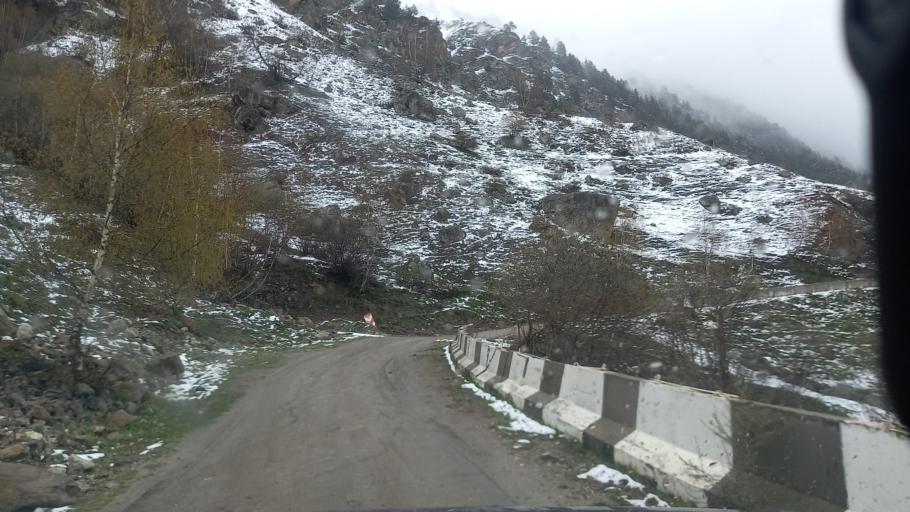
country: RU
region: Kabardino-Balkariya
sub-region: El'brusskiy Rayon
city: El'brus
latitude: 43.2254
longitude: 42.6736
